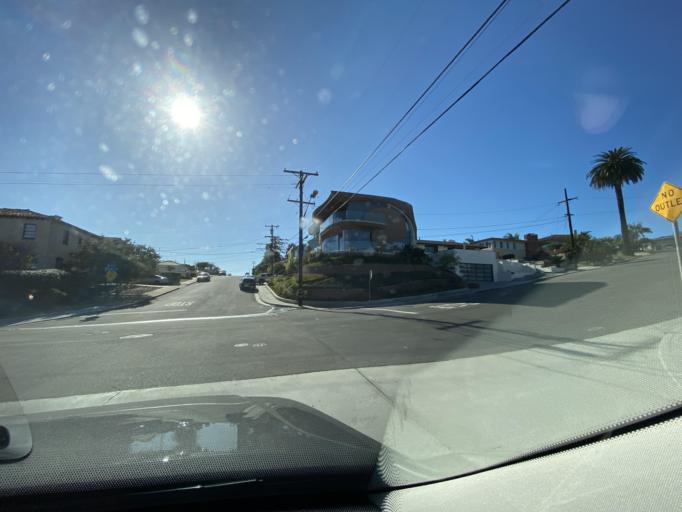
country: US
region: California
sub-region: San Diego County
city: Coronado
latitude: 32.7311
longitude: -117.2297
